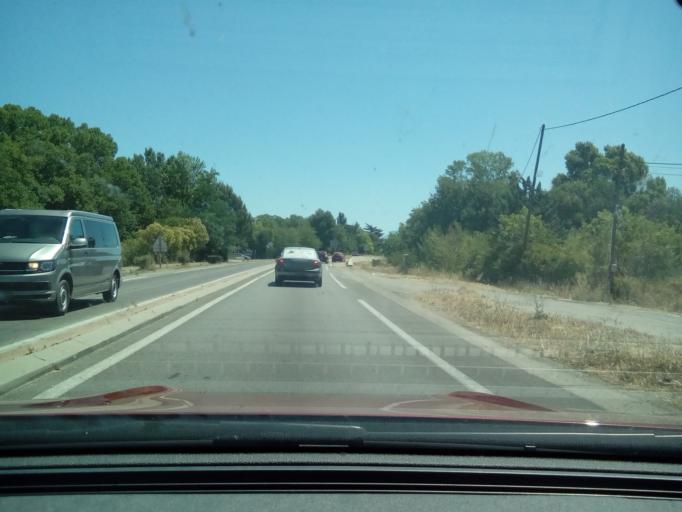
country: FR
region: Provence-Alpes-Cote d'Azur
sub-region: Departement des Bouches-du-Rhone
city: Chateauneuf-le-Rouge
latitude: 43.4786
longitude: 5.5670
